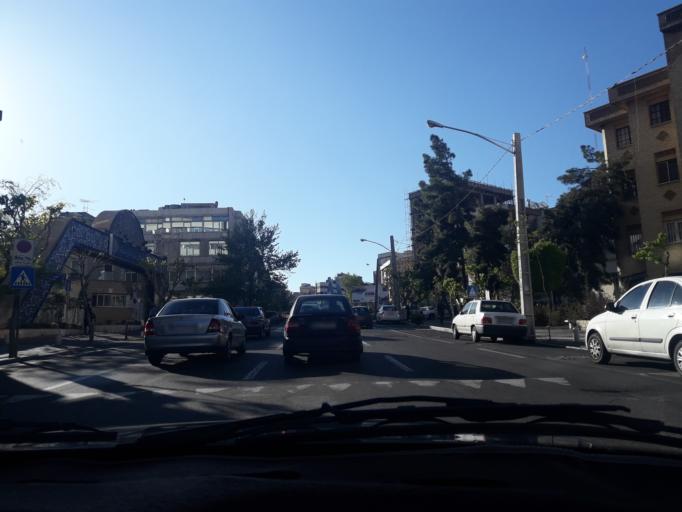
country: IR
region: Tehran
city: Tehran
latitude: 35.7207
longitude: 51.4032
